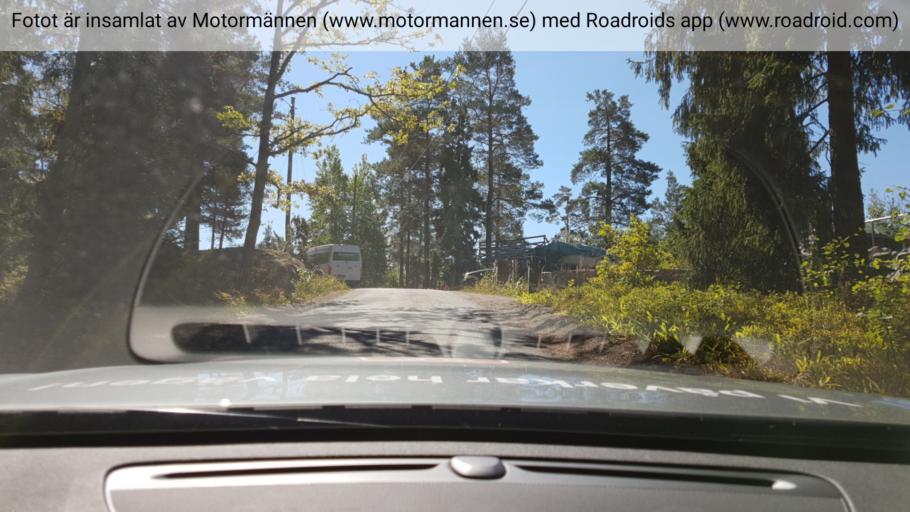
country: SE
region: Stockholm
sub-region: Nacka Kommun
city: Saltsjobaden
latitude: 59.2212
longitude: 18.3118
